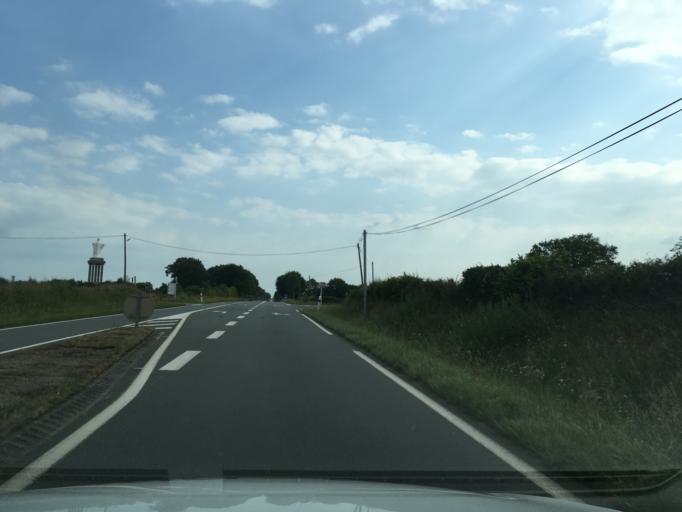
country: FR
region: Poitou-Charentes
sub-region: Departement des Deux-Sevres
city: Le Tallud
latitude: 46.6136
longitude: -0.2842
